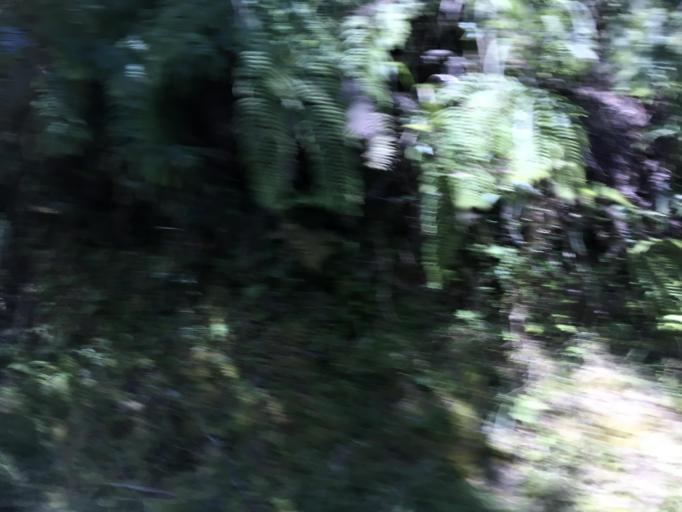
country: TW
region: Taiwan
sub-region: Yilan
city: Yilan
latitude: 24.5234
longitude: 121.5196
